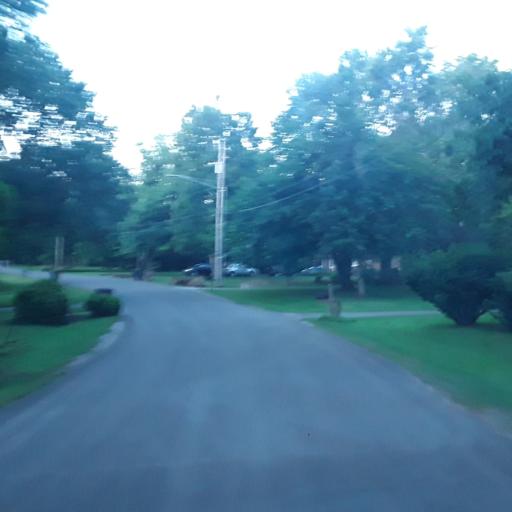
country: US
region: Tennessee
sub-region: Davidson County
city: Oak Hill
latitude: 36.0693
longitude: -86.7664
